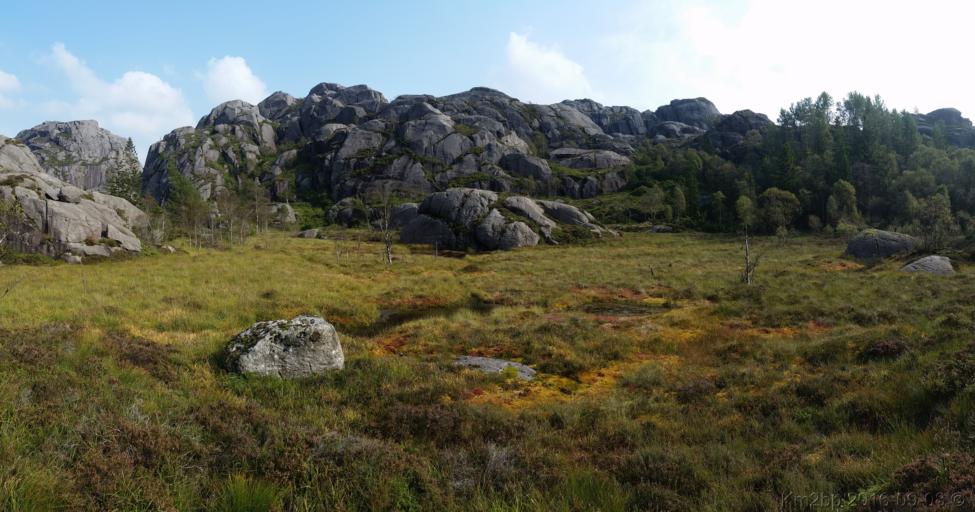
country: NO
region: Rogaland
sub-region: Sokndal
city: Hauge i Dalane
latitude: 58.3266
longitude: 6.3391
